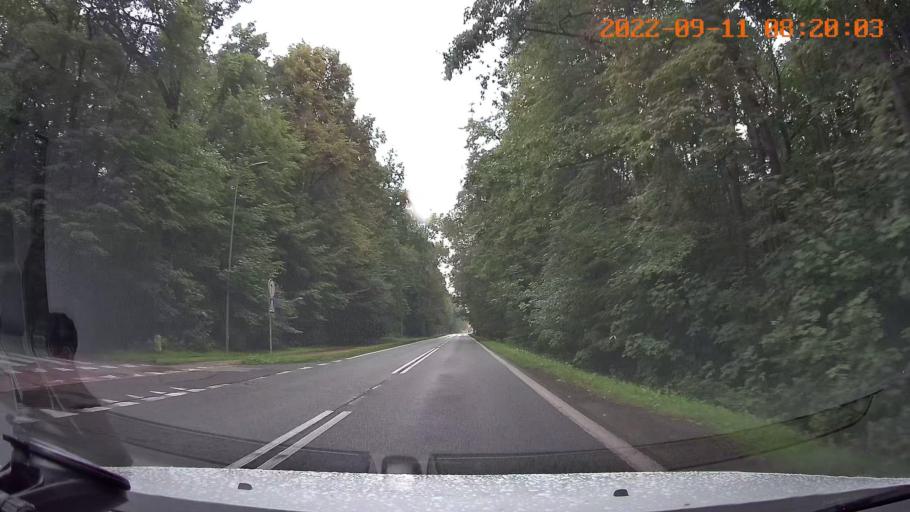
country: PL
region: Silesian Voivodeship
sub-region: Tychy
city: Tychy
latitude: 50.1560
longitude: 19.0084
